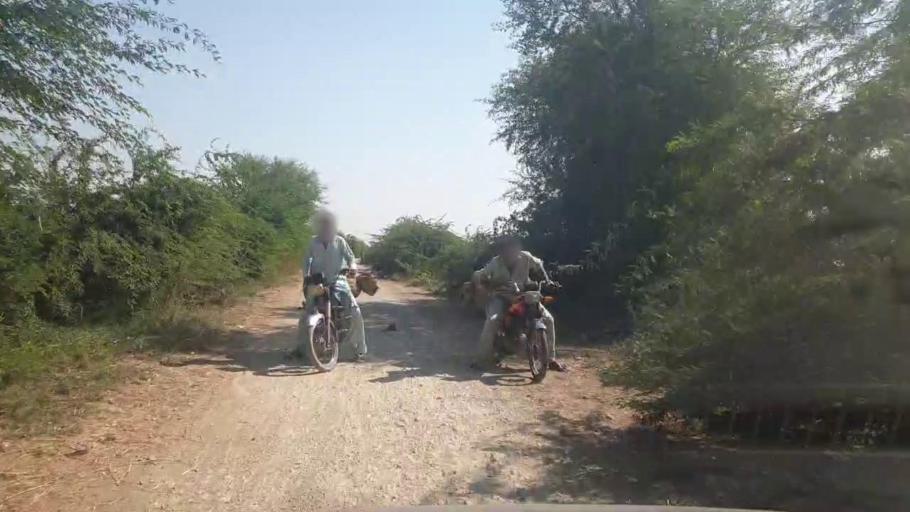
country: PK
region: Sindh
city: Badin
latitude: 24.5829
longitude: 68.8452
